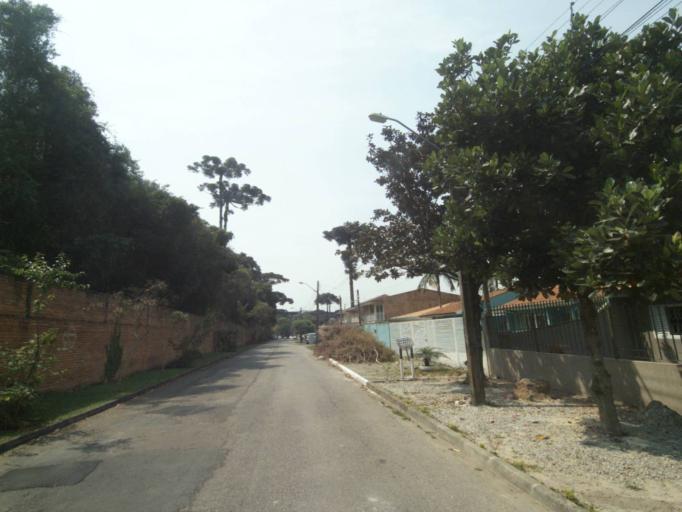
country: BR
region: Parana
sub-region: Sao Jose Dos Pinhais
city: Sao Jose dos Pinhais
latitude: -25.4911
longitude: -49.2110
